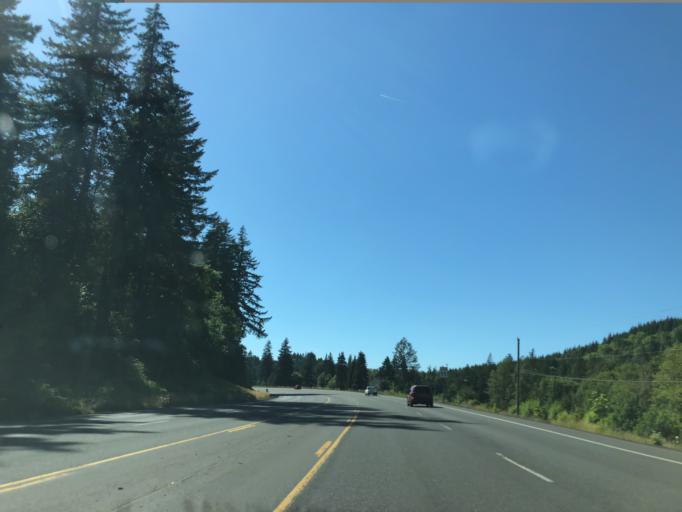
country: US
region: Oregon
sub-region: Linn County
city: Sweet Home
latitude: 44.4040
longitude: -122.7496
